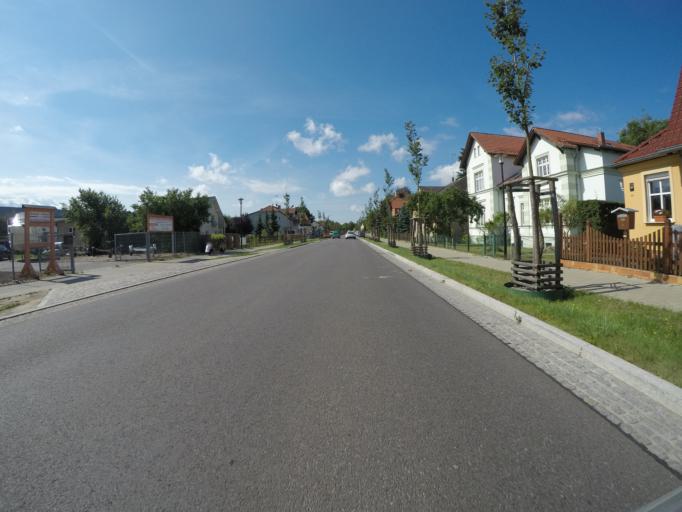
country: DE
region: Brandenburg
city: Rheinsberg
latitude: 53.1045
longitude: 12.8938
